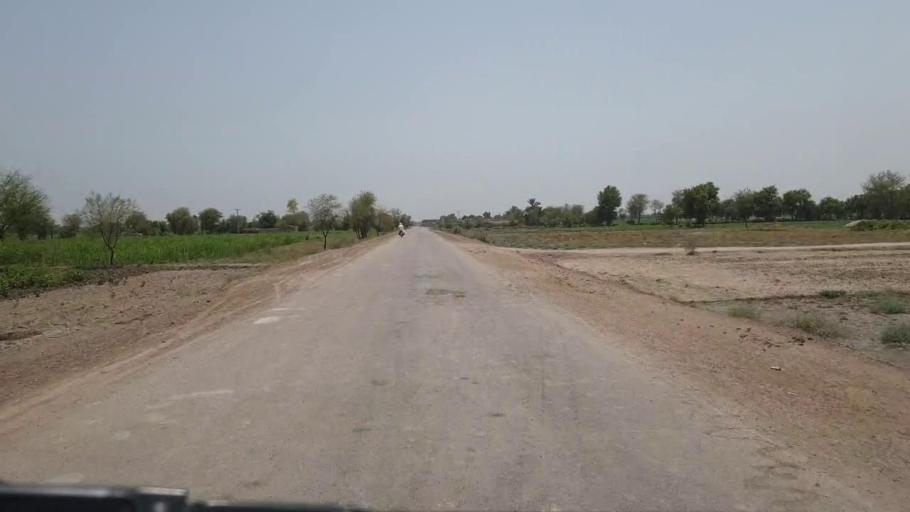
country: PK
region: Sindh
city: Daulatpur
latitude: 26.4472
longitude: 68.1164
